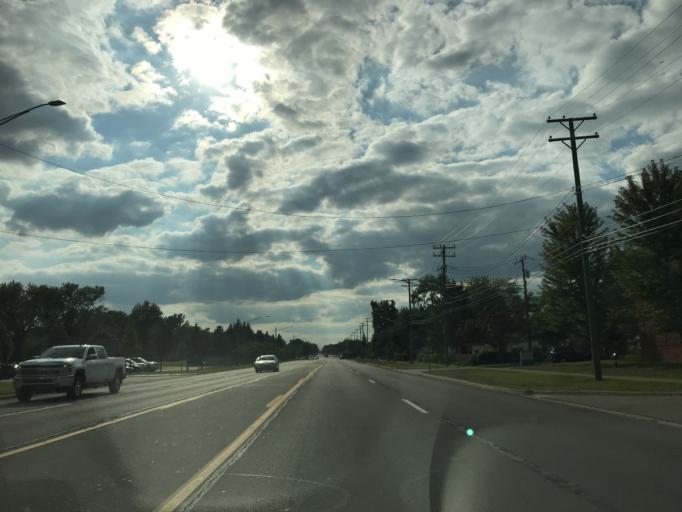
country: US
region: Michigan
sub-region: Wayne County
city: Redford
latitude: 42.4142
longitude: -83.2905
